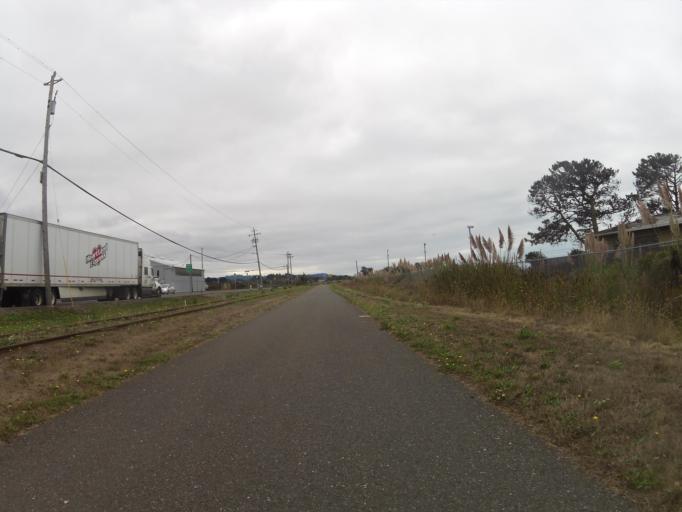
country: US
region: California
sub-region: Humboldt County
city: Bayview
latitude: 40.7923
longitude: -124.1848
